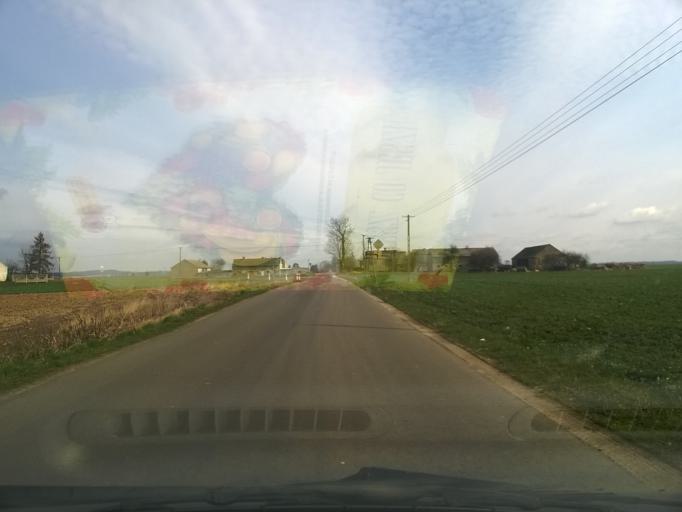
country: PL
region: Greater Poland Voivodeship
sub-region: Powiat wagrowiecki
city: Golancz
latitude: 52.9630
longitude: 17.3394
